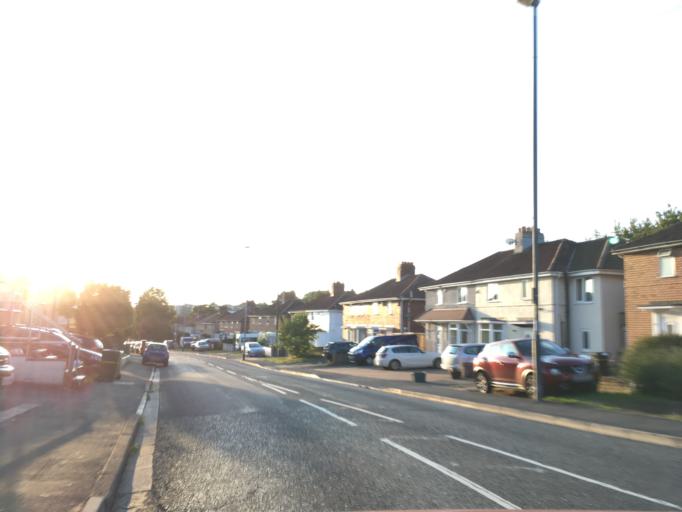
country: GB
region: England
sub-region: South Gloucestershire
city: Kingswood
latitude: 51.4531
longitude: -2.5417
